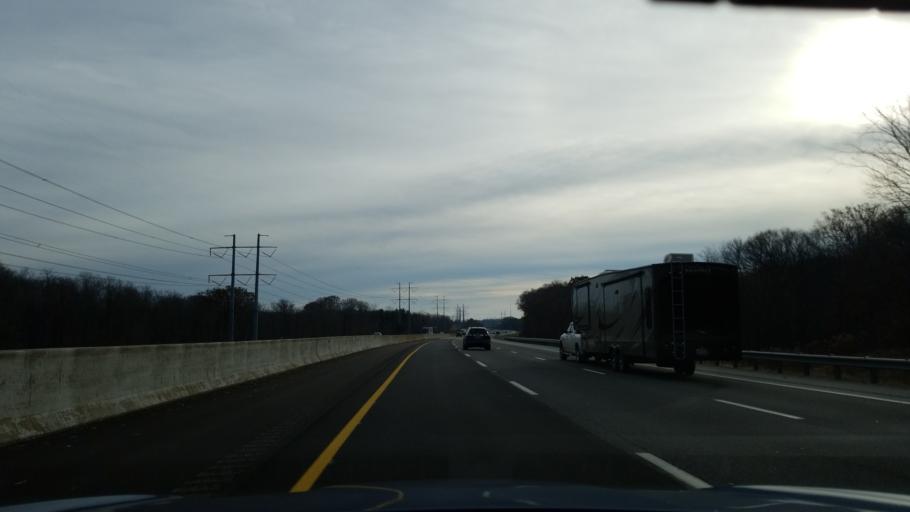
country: US
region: Ohio
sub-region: Cuyahoga County
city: Broadview Heights
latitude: 41.3019
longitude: -81.7037
